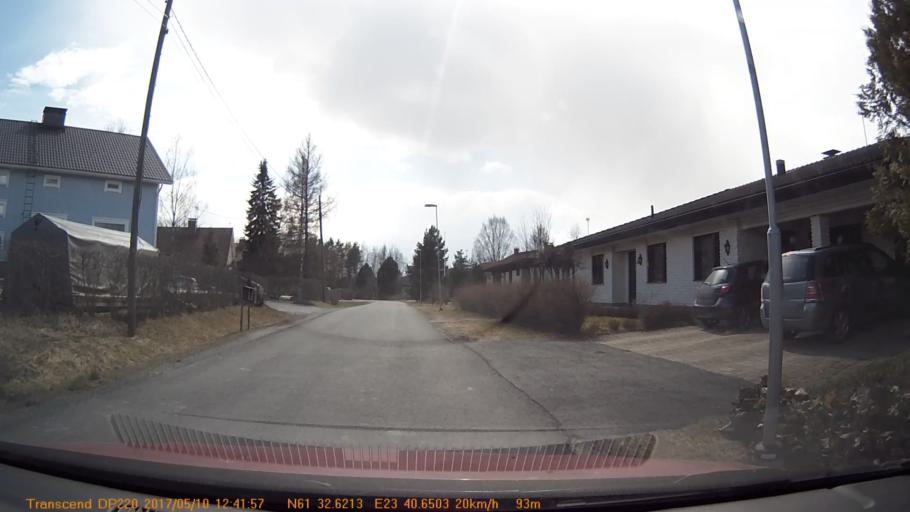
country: FI
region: Pirkanmaa
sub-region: Tampere
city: Yloejaervi
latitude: 61.5436
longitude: 23.6774
